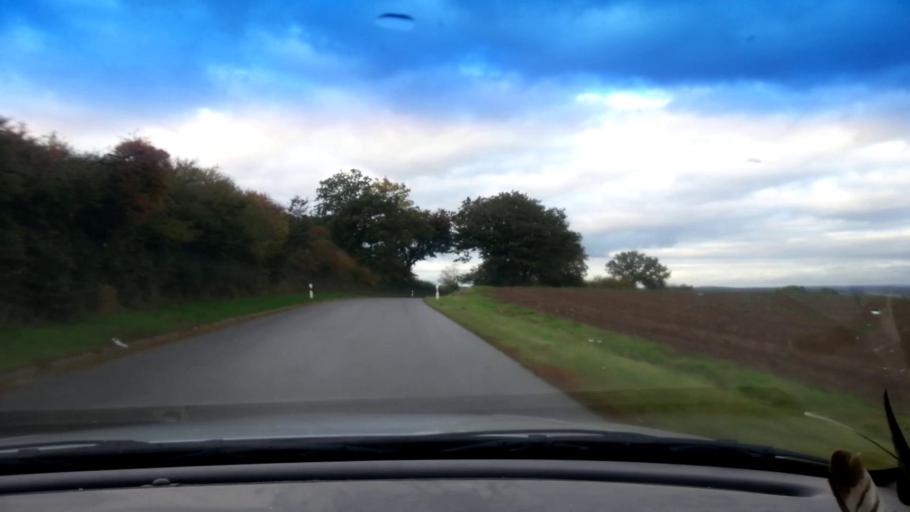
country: DE
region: Bavaria
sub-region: Upper Franconia
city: Burgwindheim
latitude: 49.8130
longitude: 10.6639
